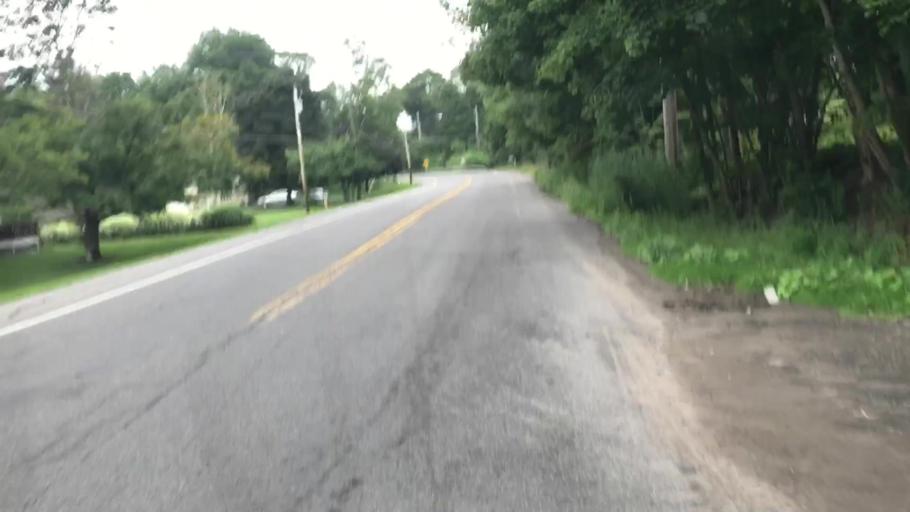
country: US
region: New York
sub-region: Onondaga County
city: Camillus
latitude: 43.0740
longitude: -76.3293
